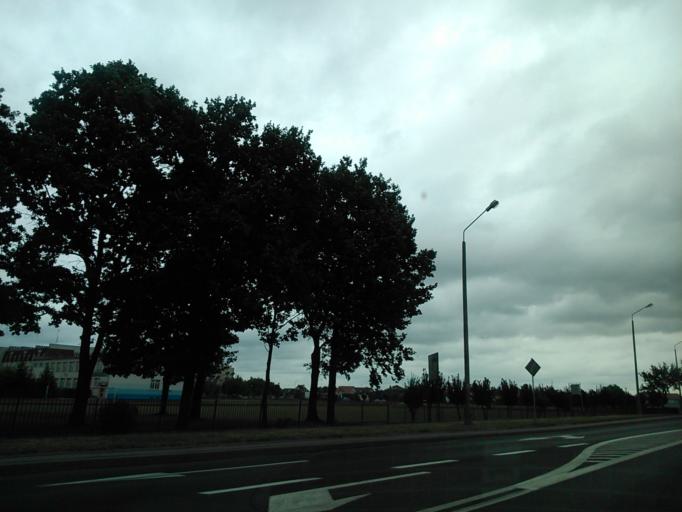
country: PL
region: Kujawsko-Pomorskie
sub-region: Powiat inowroclawski
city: Kruszwica
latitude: 52.6742
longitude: 18.3360
